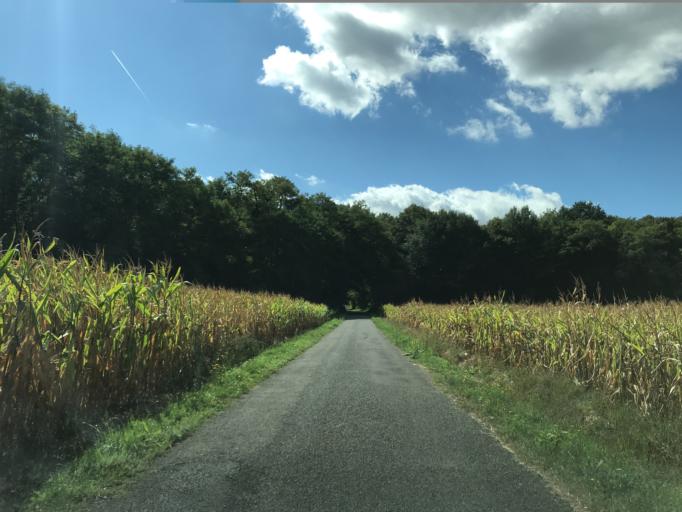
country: FR
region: Haute-Normandie
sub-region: Departement de l'Eure
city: Saint-Just
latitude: 49.1491
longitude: 1.4061
